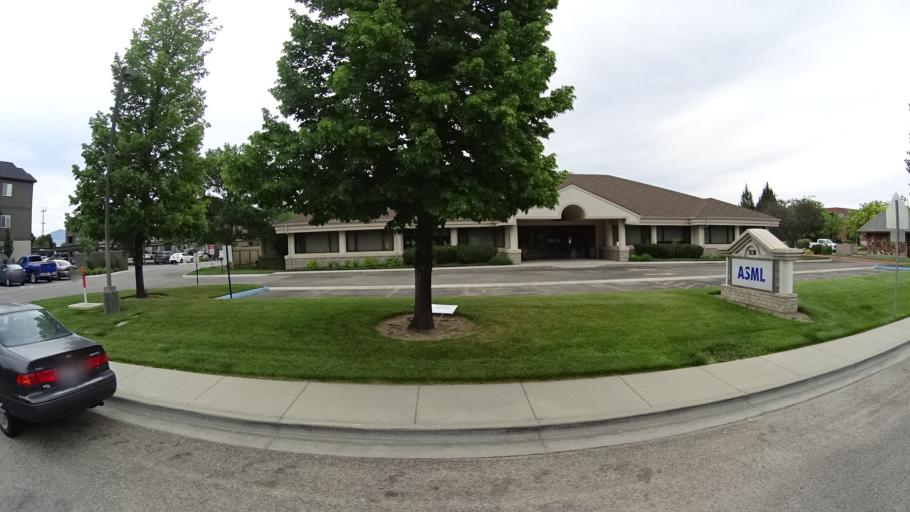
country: US
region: Idaho
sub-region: Ada County
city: Boise
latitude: 43.5743
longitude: -116.2235
